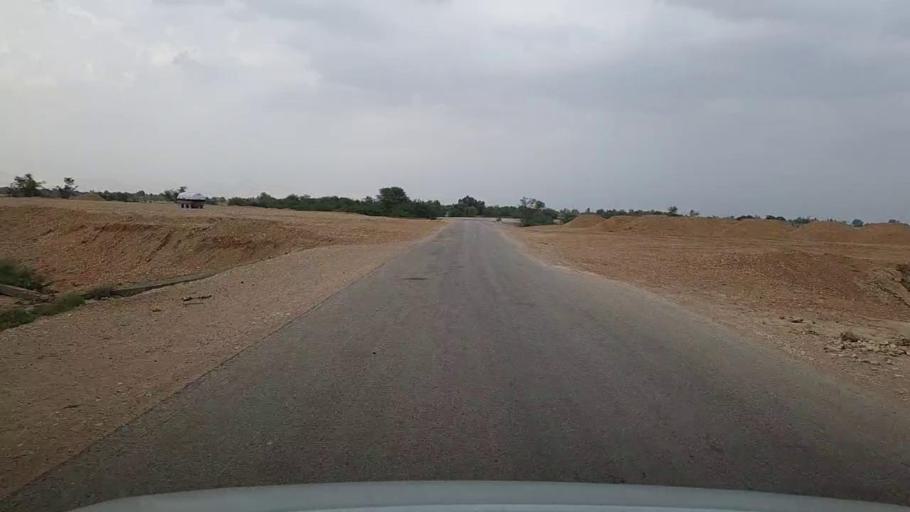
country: PK
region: Sindh
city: Sehwan
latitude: 26.3392
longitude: 67.7268
